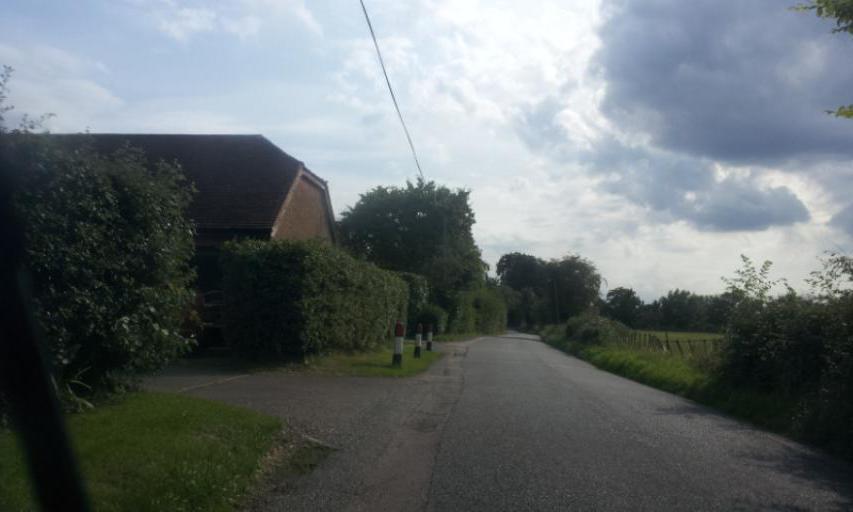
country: GB
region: England
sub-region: Kent
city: Hadlow
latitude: 51.2306
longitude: 0.3327
